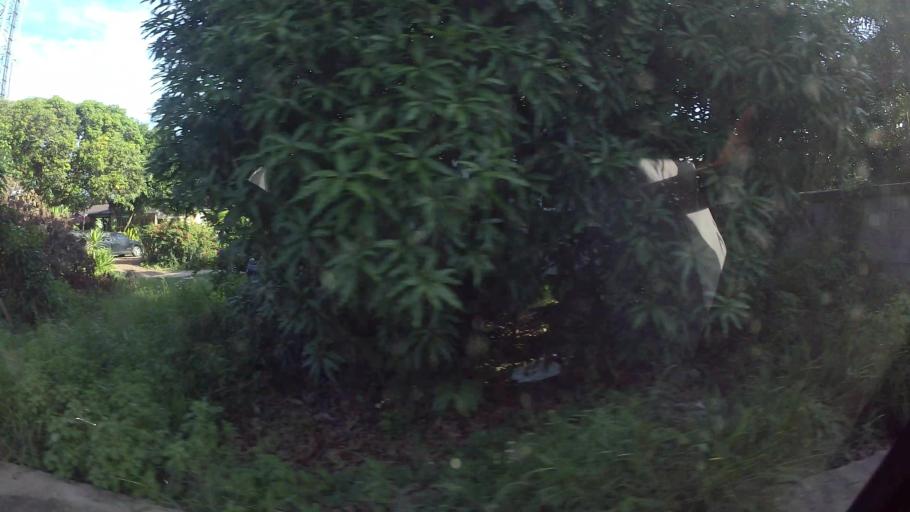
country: TH
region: Chon Buri
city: Sattahip
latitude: 12.6718
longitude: 100.9132
